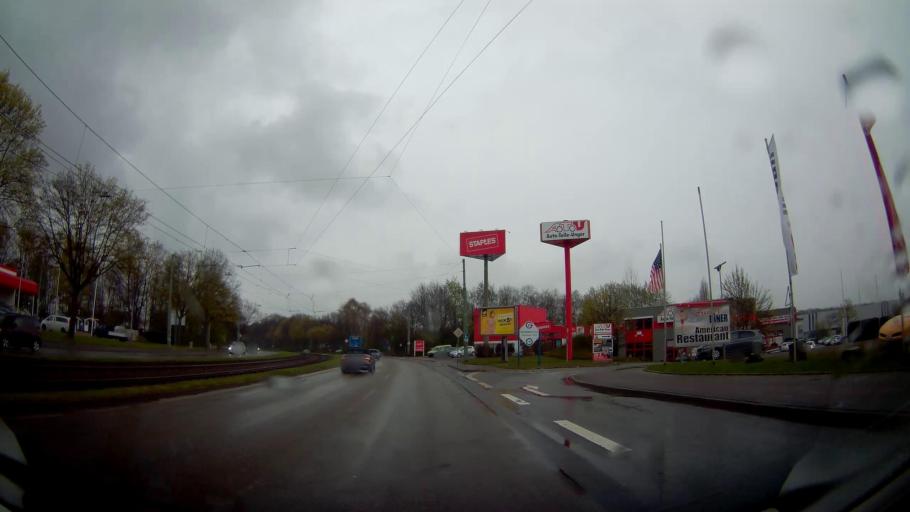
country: DE
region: North Rhine-Westphalia
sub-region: Regierungsbezirk Arnsberg
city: Bochum
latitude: 51.4991
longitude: 7.2588
